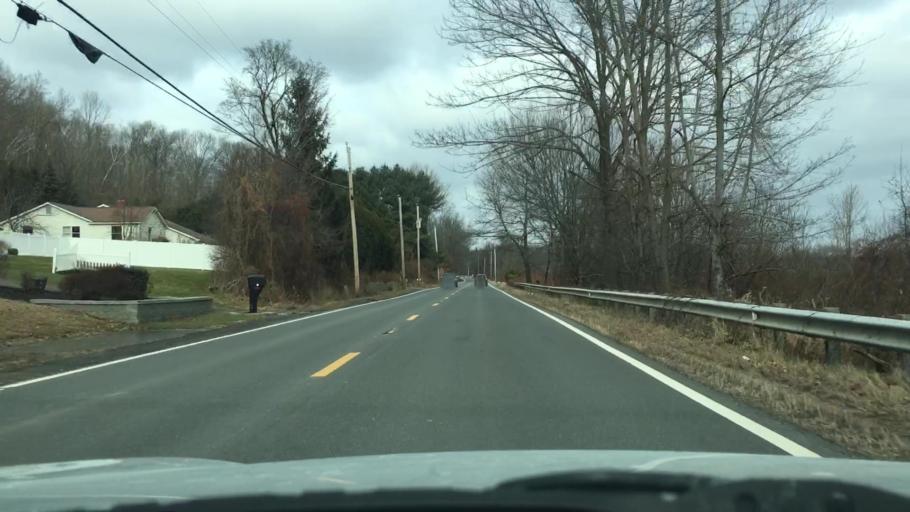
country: US
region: Connecticut
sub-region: Hartford County
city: North Granby
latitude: 42.0060
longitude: -72.7954
